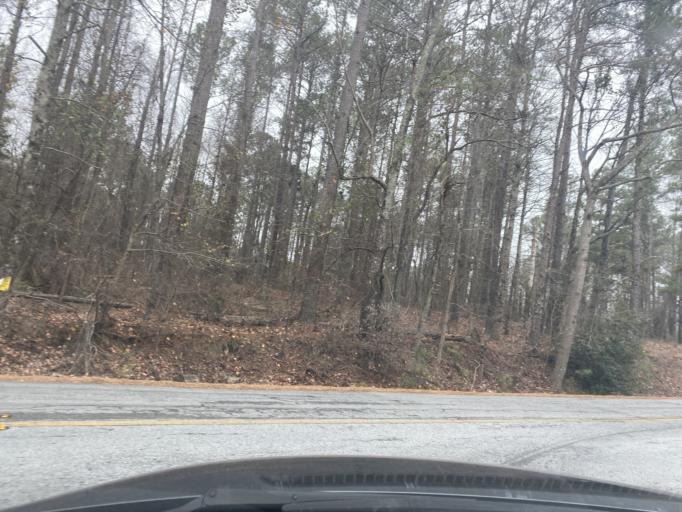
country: US
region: Georgia
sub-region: DeKalb County
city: Pine Mountain
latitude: 33.6866
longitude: -84.1431
